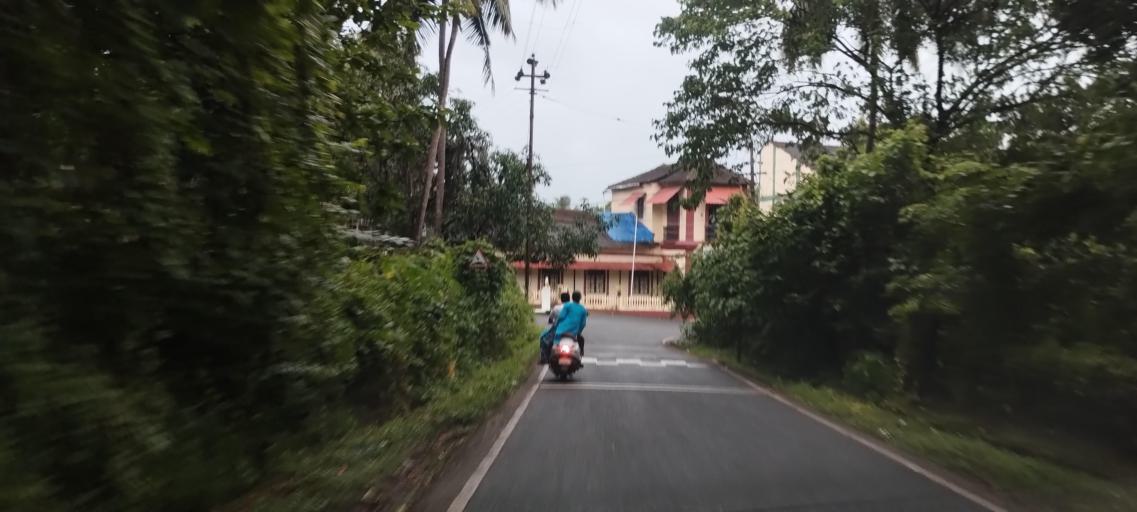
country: IN
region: Goa
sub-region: North Goa
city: Jua
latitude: 15.5266
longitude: 73.9029
